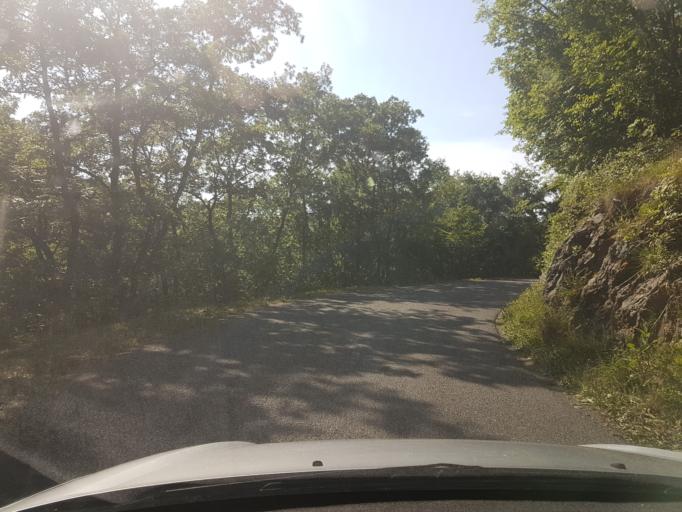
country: SI
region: Divaca
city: Divaca
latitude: 45.7486
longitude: 13.9972
